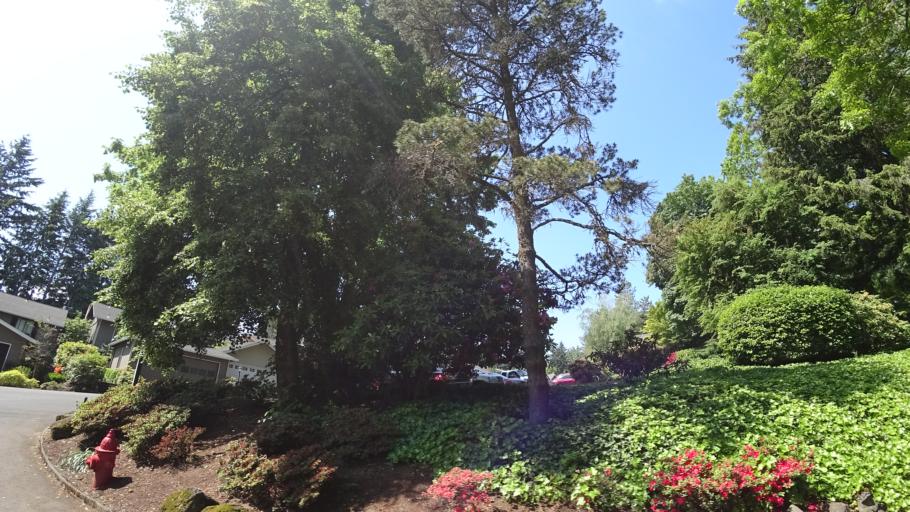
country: US
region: Oregon
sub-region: Clackamas County
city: Lake Oswego
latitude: 45.4263
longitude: -122.7112
